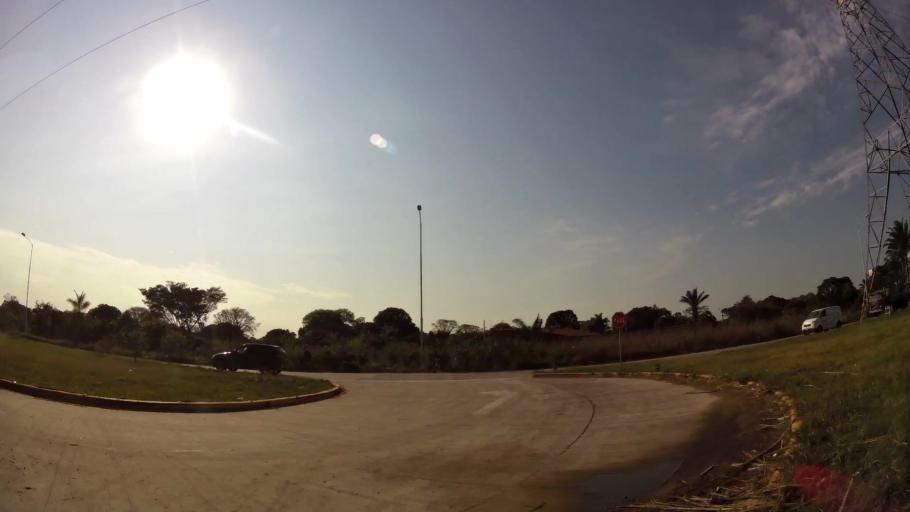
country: BO
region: Santa Cruz
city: Santa Cruz de la Sierra
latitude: -17.7140
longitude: -63.1273
